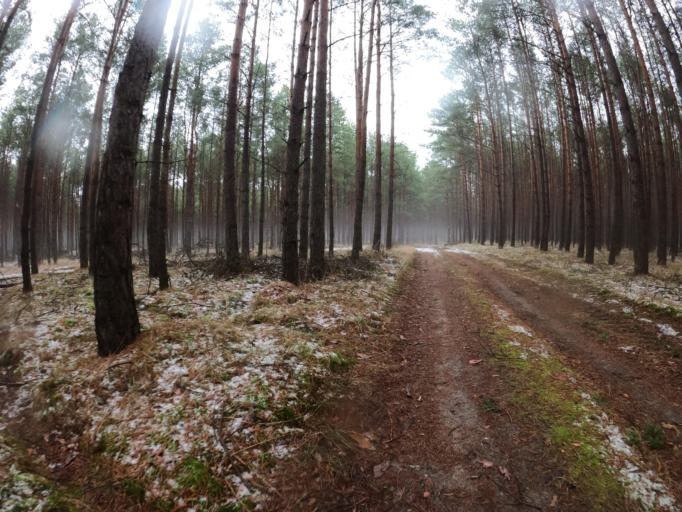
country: PL
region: Lubusz
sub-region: Powiat slubicki
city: Cybinka
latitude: 52.2042
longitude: 14.9304
